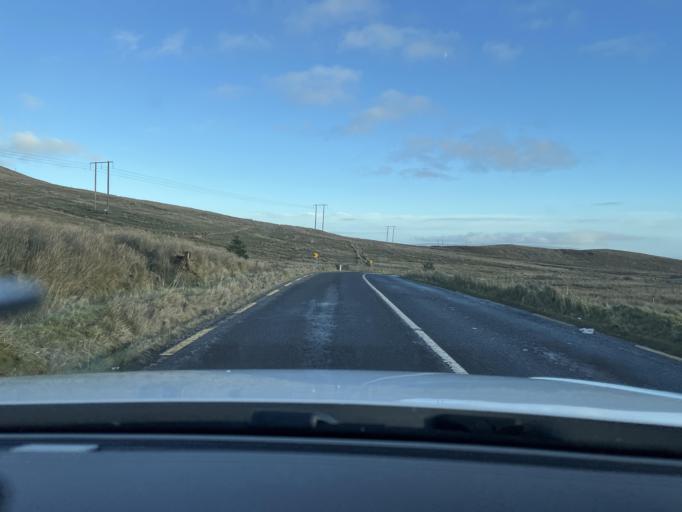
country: IE
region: Ulster
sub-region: An Cabhan
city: Ballyconnell
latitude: 54.1691
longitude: -7.8168
